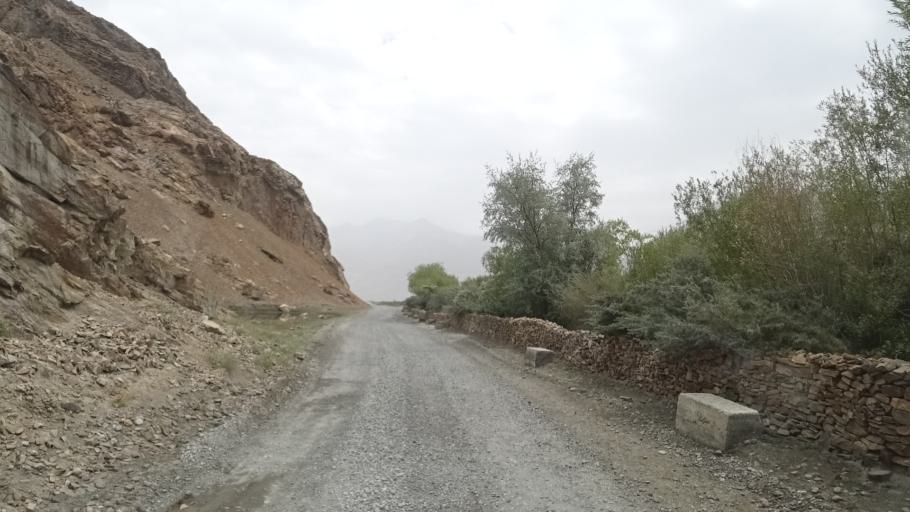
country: AF
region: Badakhshan
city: Khandud
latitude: 37.0219
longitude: 72.5994
